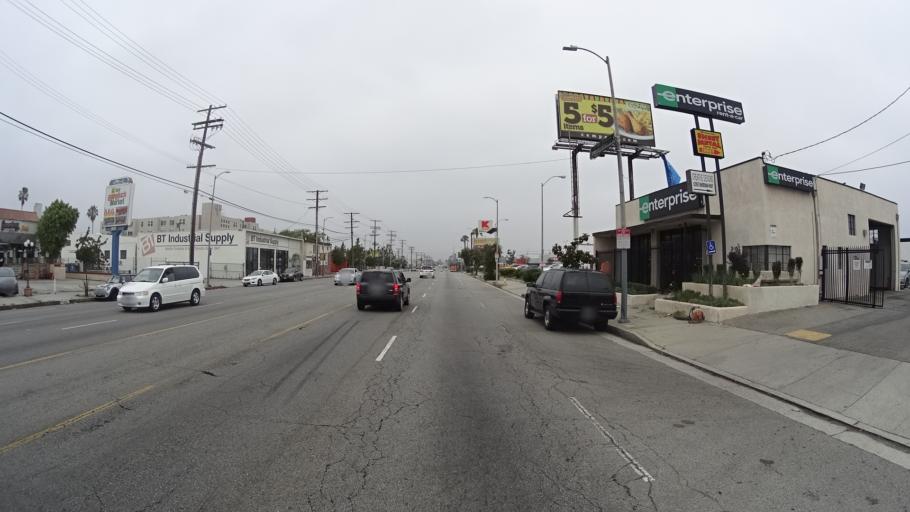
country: US
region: California
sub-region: Los Angeles County
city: Van Nuys
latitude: 34.2013
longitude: -118.4156
